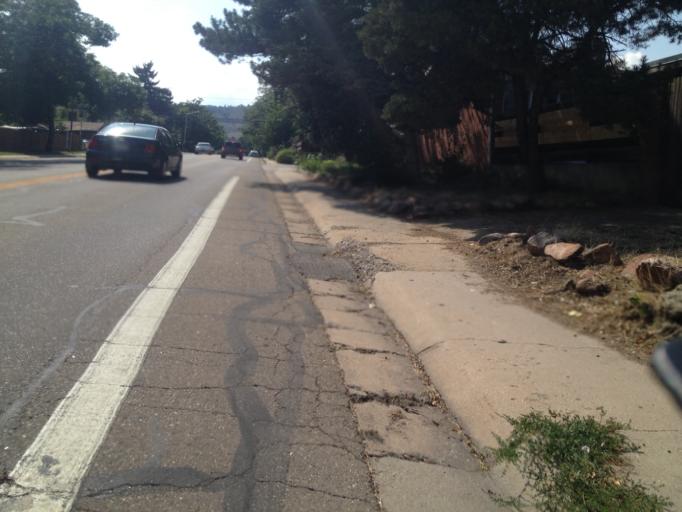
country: US
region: Colorado
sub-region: Boulder County
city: Boulder
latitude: 40.0268
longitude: -105.2753
